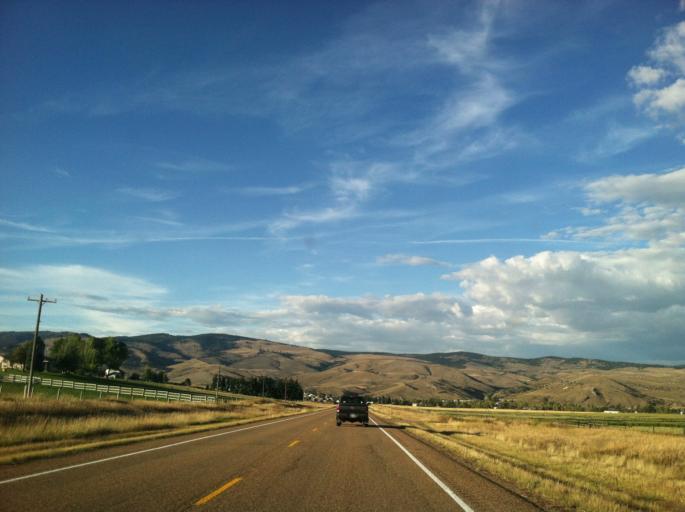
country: US
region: Montana
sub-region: Granite County
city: Philipsburg
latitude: 46.6481
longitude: -113.1631
